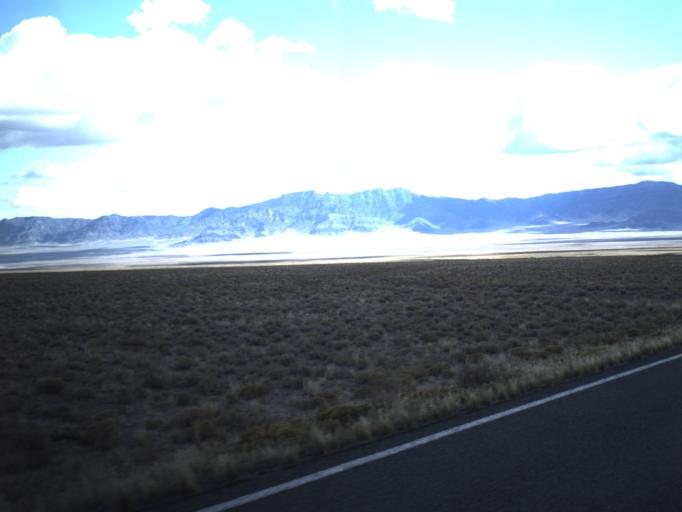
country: US
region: Utah
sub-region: Beaver County
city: Milford
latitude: 38.5701
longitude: -113.7842
